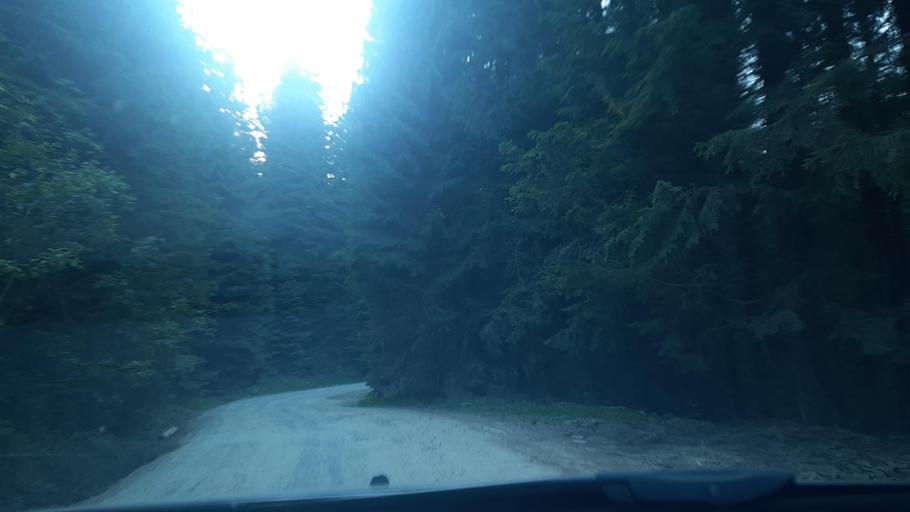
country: RO
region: Alba
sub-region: Comuna Sugag
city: Sugag
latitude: 45.5782
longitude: 23.6086
